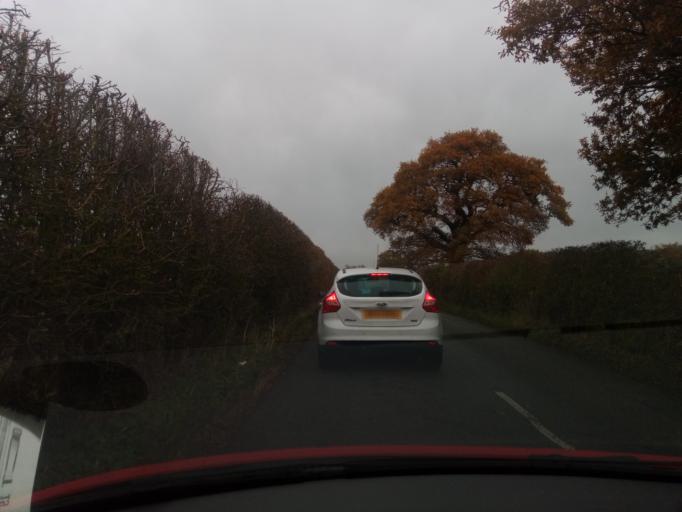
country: GB
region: England
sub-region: Derbyshire
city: Borrowash
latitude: 52.9395
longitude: -1.4062
